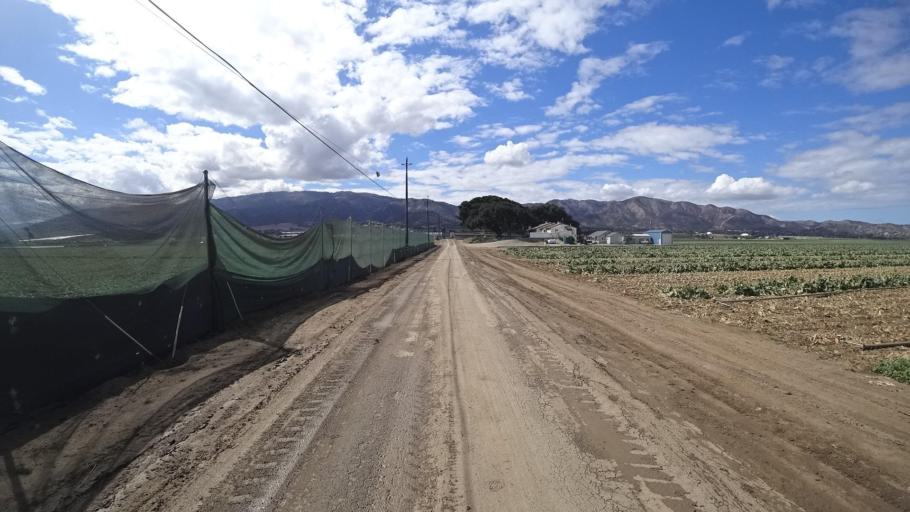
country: US
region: California
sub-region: Monterey County
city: Chualar
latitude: 36.6015
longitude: -121.6036
